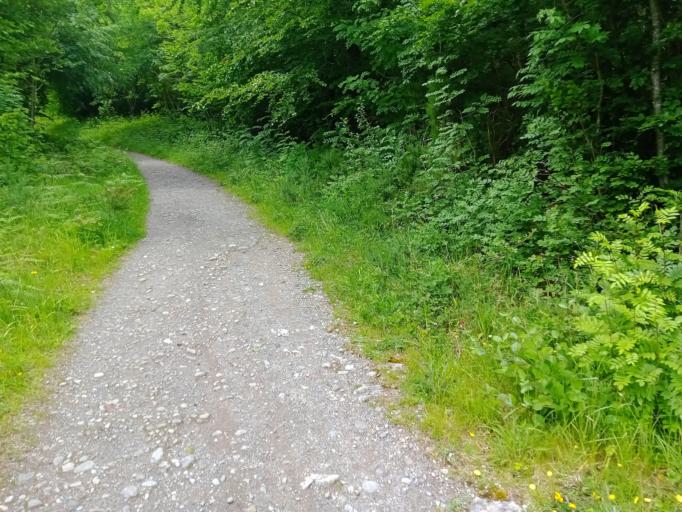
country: IE
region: Leinster
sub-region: Laois
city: Stradbally
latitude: 52.9957
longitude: -7.1171
